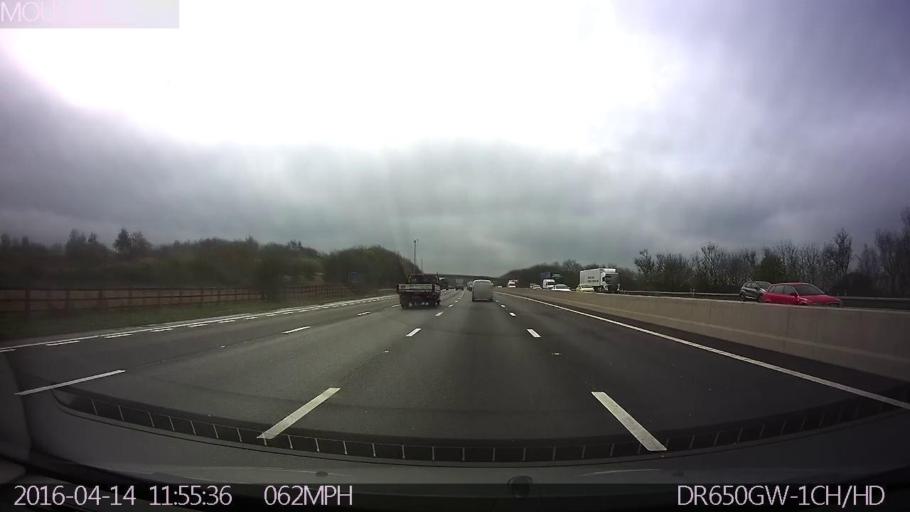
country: GB
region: England
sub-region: Derbyshire
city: Tibshelf
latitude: 53.1424
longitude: -1.3310
